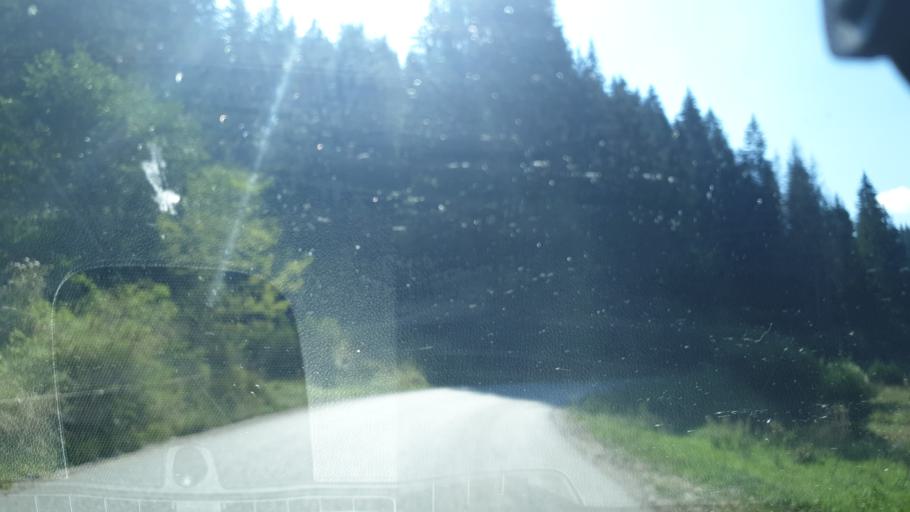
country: RS
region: Central Serbia
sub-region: Zlatiborski Okrug
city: Nova Varos
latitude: 43.4495
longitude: 19.8486
